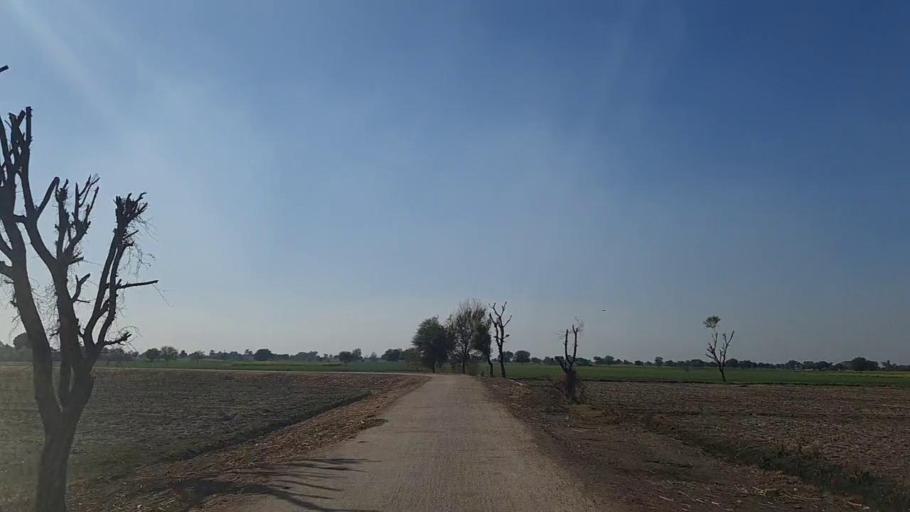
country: PK
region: Sindh
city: Shahpur Chakar
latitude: 26.2187
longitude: 68.6040
